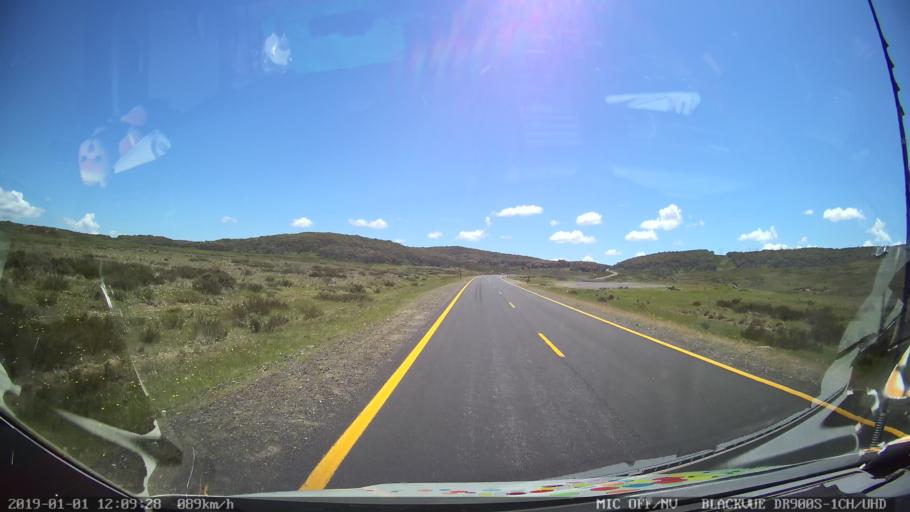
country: AU
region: New South Wales
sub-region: Tumut Shire
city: Tumut
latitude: -35.8068
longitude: 148.4960
